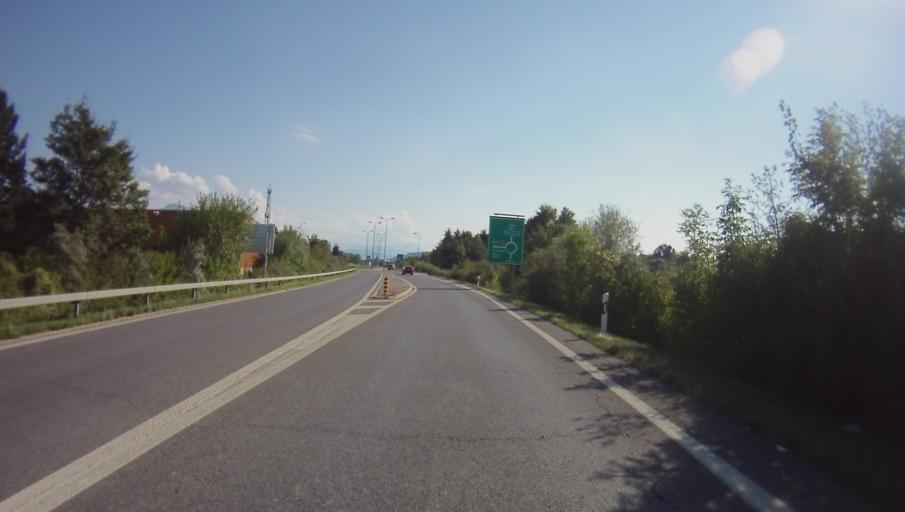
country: CH
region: Zug
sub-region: Zug
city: Steinhausen
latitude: 47.1949
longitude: 8.4739
